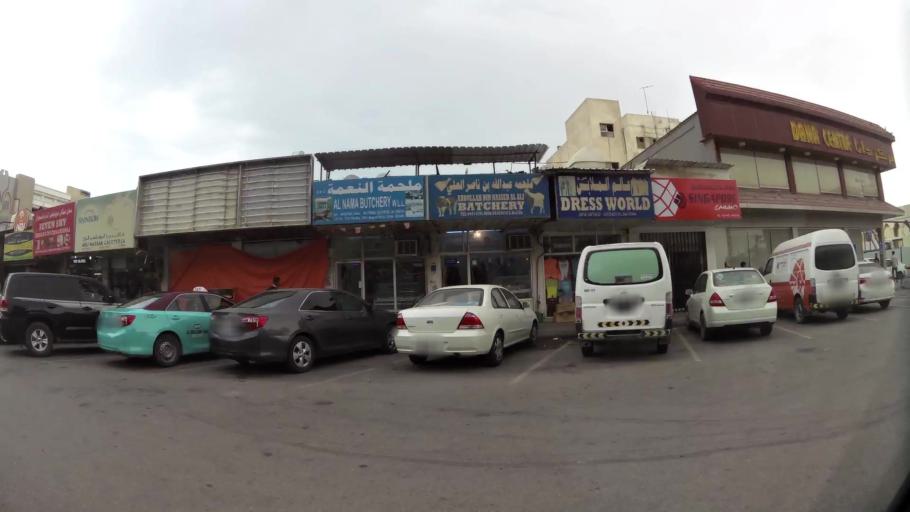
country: QA
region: Baladiyat ad Dawhah
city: Doha
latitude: 25.2879
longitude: 51.5373
